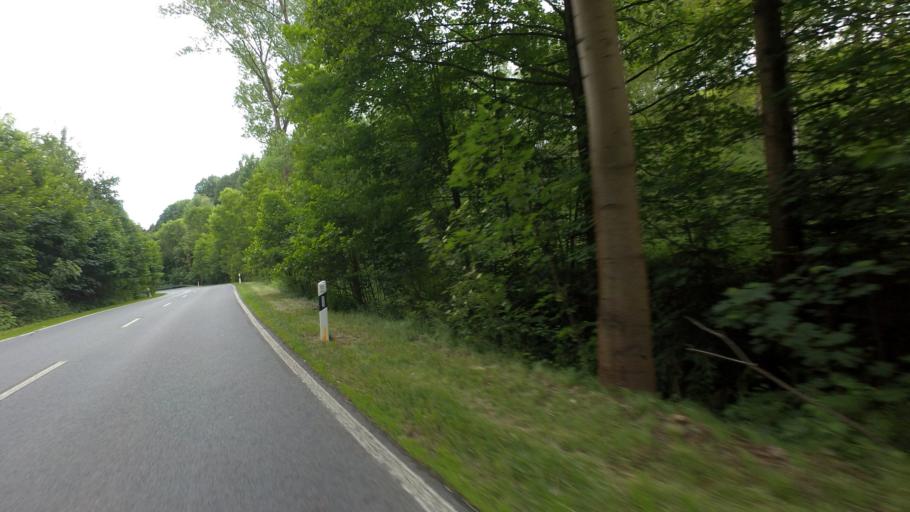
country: DE
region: Saxony
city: Sebnitz
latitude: 50.9741
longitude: 14.2598
